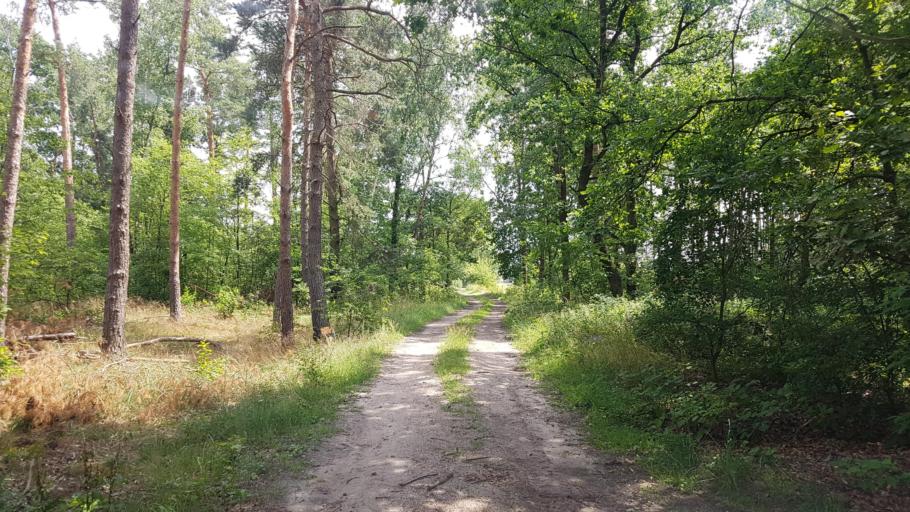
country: DE
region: Brandenburg
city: Bronkow
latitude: 51.7059
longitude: 13.8682
